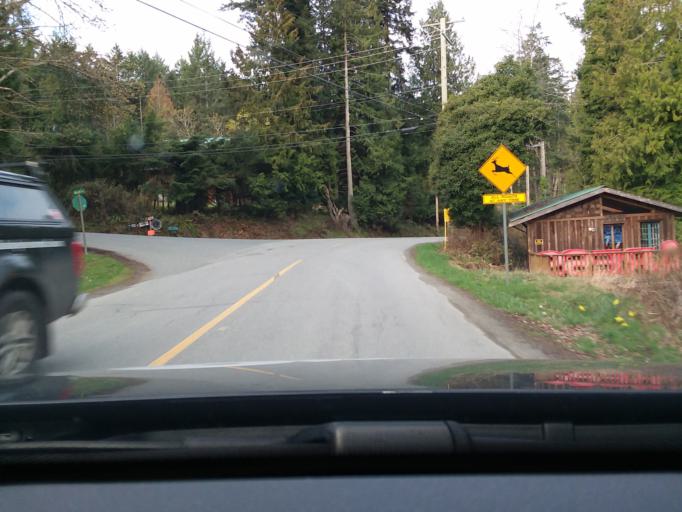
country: CA
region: British Columbia
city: North Saanich
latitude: 48.8793
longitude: -123.3227
